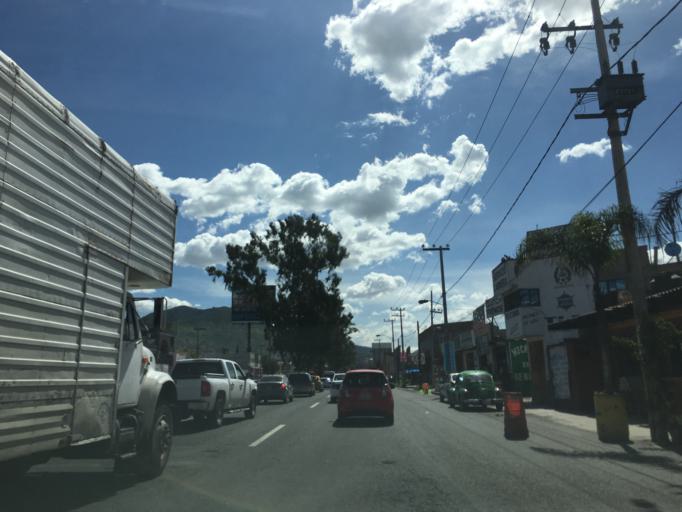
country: MX
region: Mexico
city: Ecatepec
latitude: 19.6137
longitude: -99.0443
